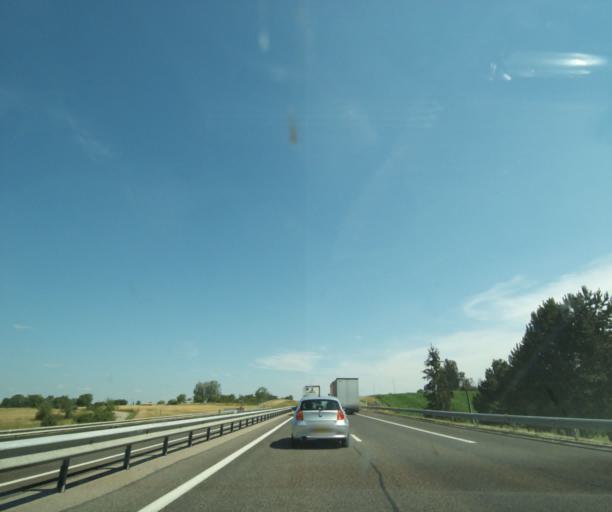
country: FR
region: Lorraine
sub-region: Departement de Meurthe-et-Moselle
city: Blenod-les-Toul
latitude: 48.5793
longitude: 5.8866
